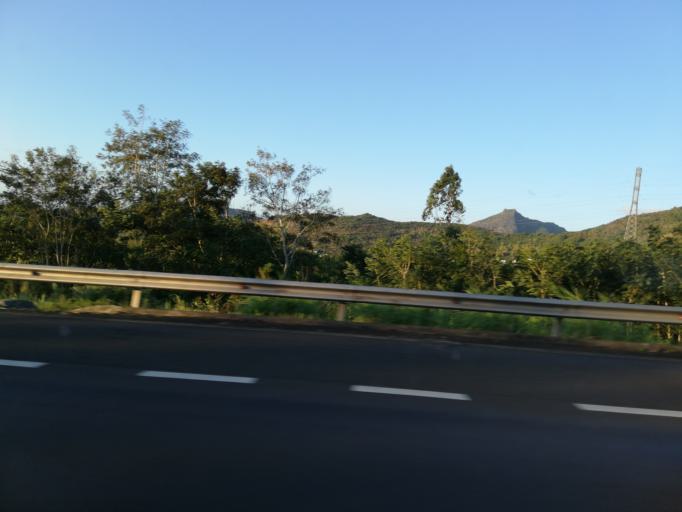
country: MU
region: Moka
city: Moka
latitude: -20.2134
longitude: 57.4794
